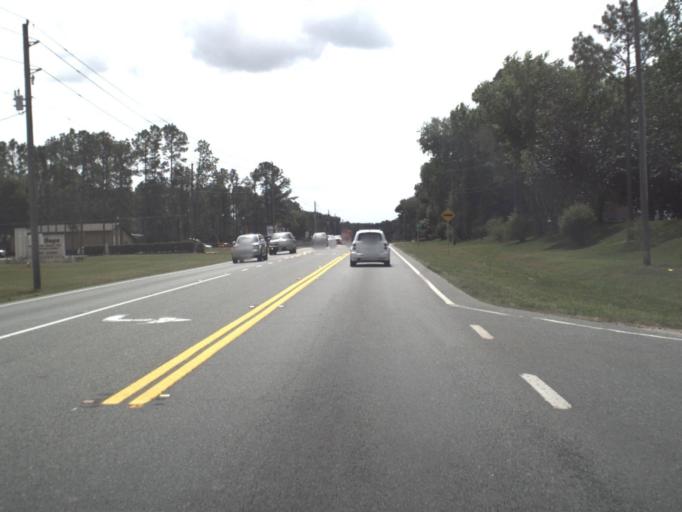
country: US
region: Florida
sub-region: Lake County
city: Mount Dora
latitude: 28.8490
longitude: -81.6339
